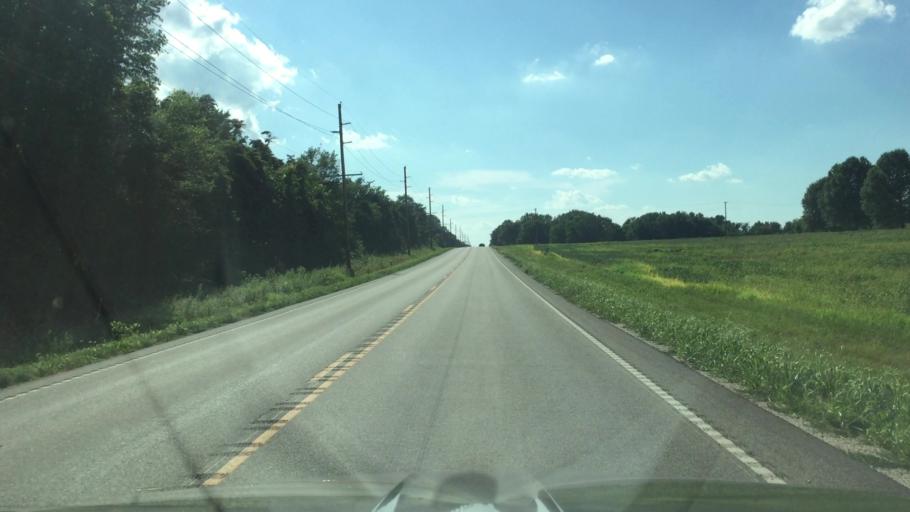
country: US
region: Missouri
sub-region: Morgan County
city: Versailles
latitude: 38.3967
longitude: -92.7260
